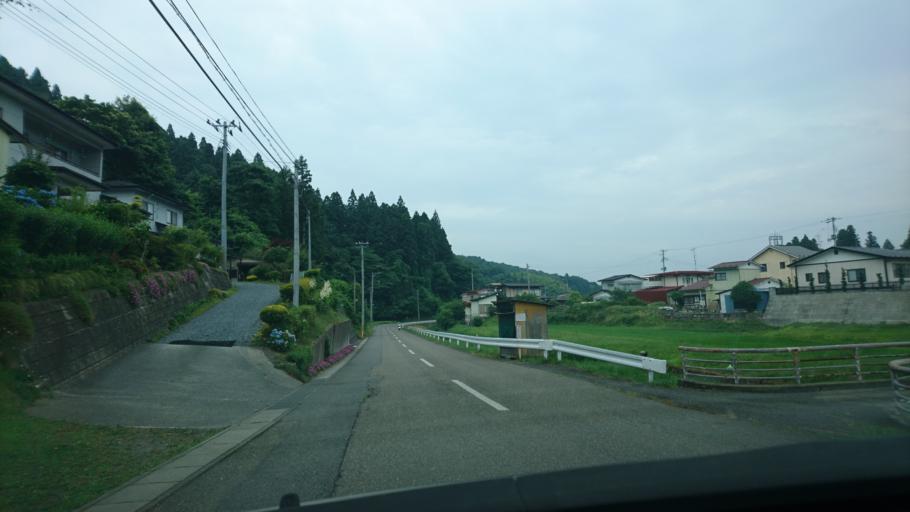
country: JP
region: Iwate
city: Ichinoseki
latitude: 38.9096
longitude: 141.1208
